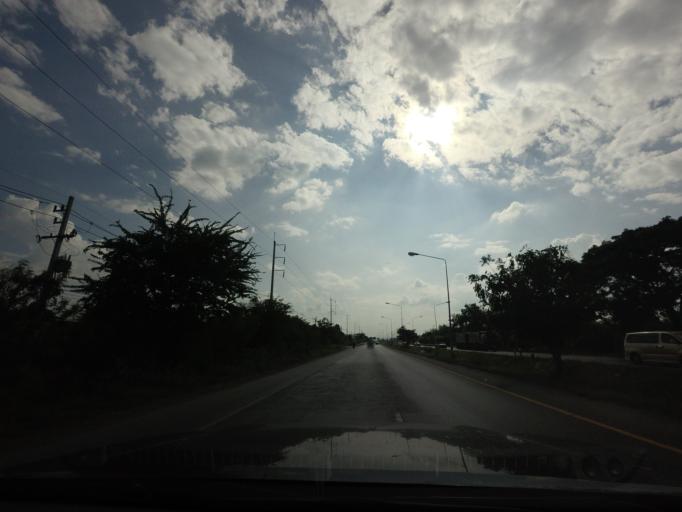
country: TH
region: Lop Buri
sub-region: Amphoe Tha Luang
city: Tha Luang
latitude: 15.0816
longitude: 101.0018
